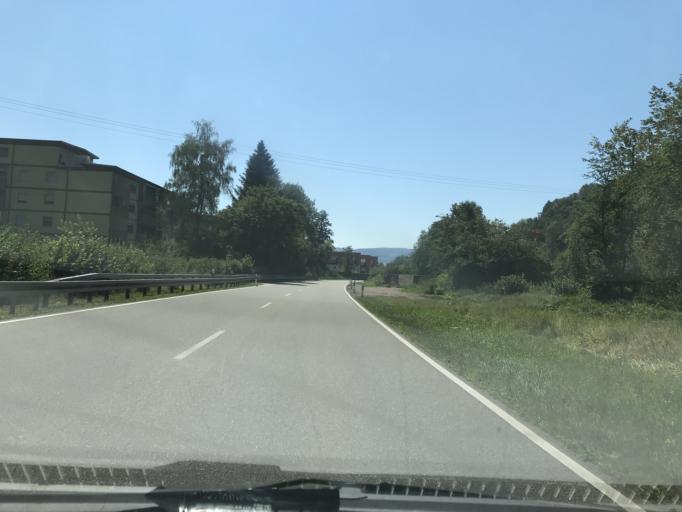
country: DE
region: Baden-Wuerttemberg
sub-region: Freiburg Region
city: Wehr
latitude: 47.6008
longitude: 7.9133
